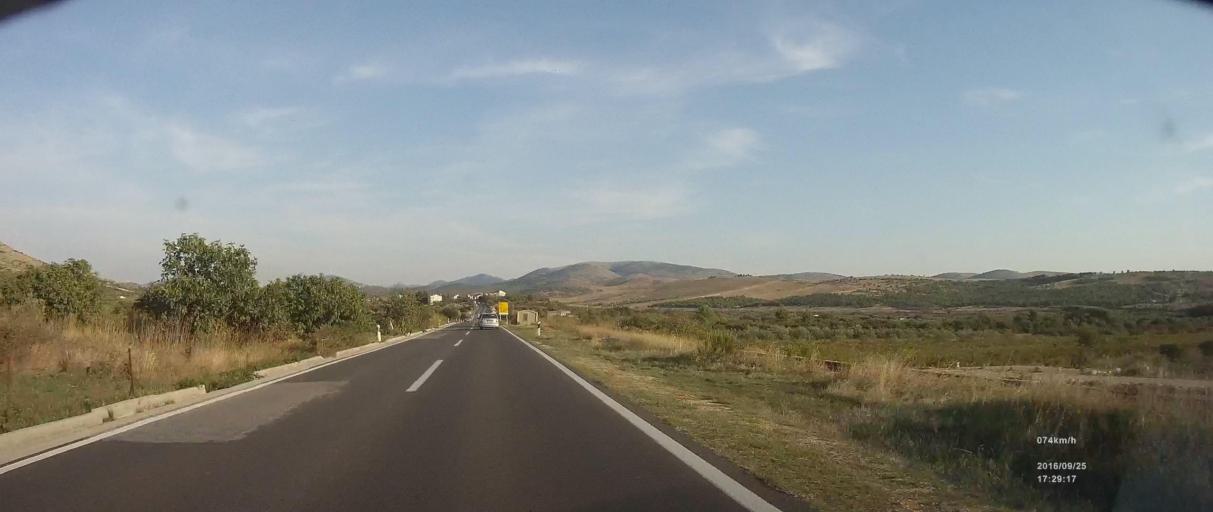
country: HR
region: Sibensko-Kniniska
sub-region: Grad Sibenik
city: Brodarica
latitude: 43.6874
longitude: 15.9637
